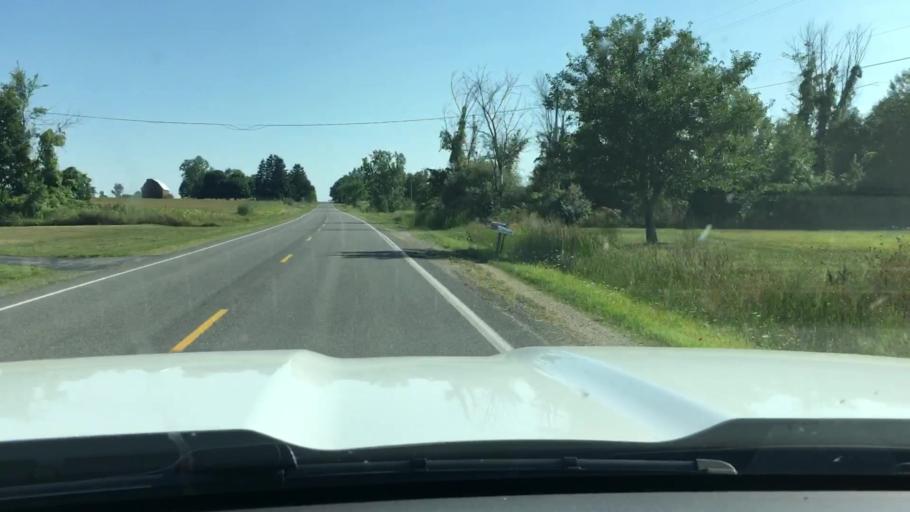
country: US
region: Michigan
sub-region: Muskegon County
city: Ravenna
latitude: 43.1702
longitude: -85.9280
